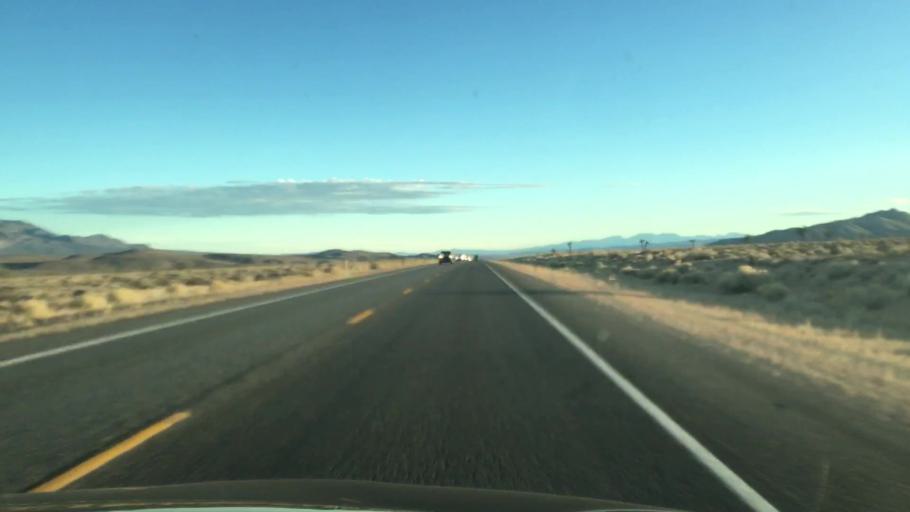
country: US
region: Nevada
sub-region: Esmeralda County
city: Goldfield
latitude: 37.6008
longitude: -117.2125
